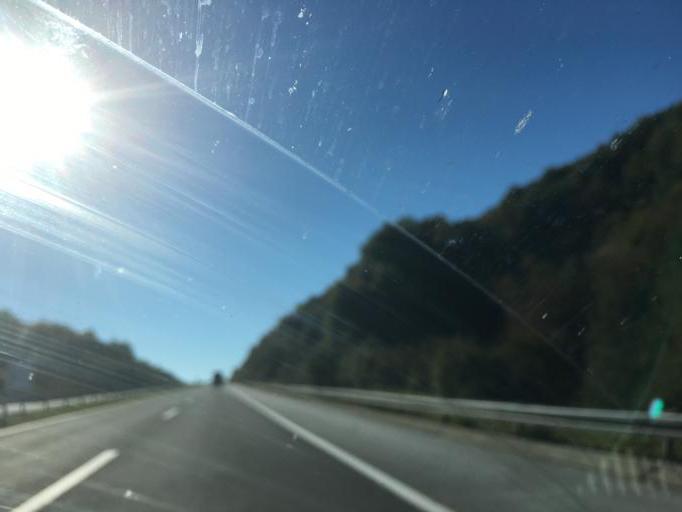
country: HR
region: Karlovacka
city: Ostarije
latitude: 45.1826
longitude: 15.2714
